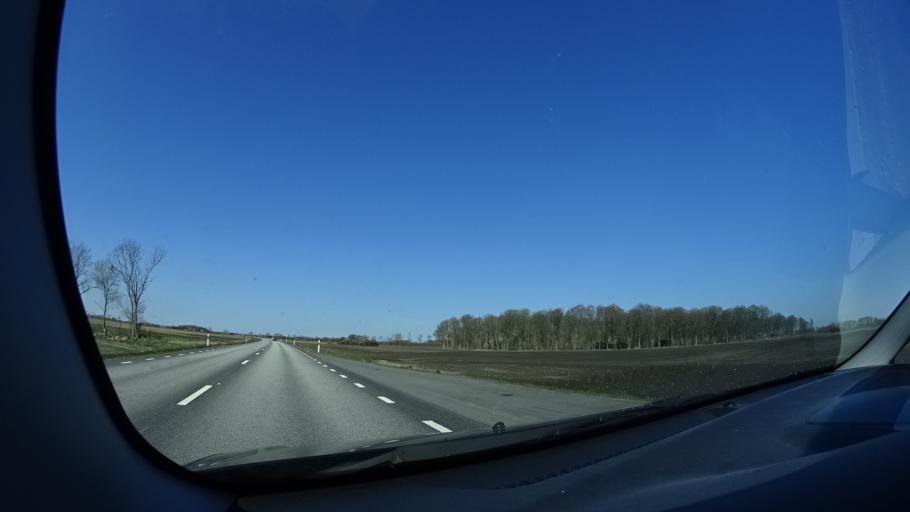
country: SE
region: Skane
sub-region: Angelholms Kommun
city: Strovelstorp
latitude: 56.2074
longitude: 12.7604
